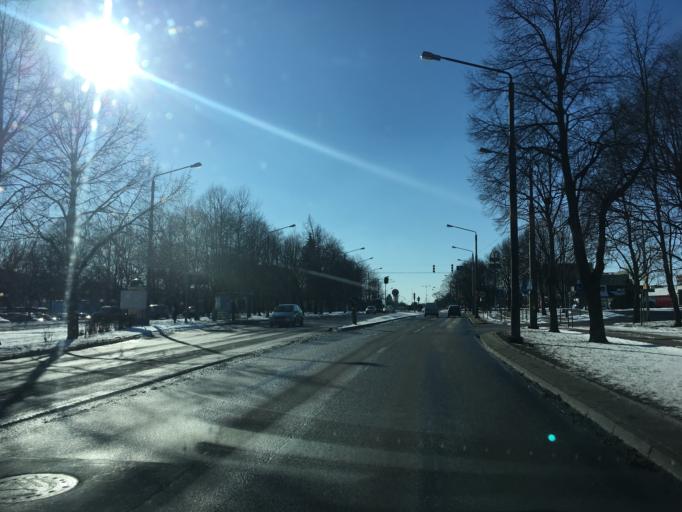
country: PL
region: Pomeranian Voivodeship
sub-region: Powiat slupski
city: Kobylnica
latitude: 54.4593
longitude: 16.9972
